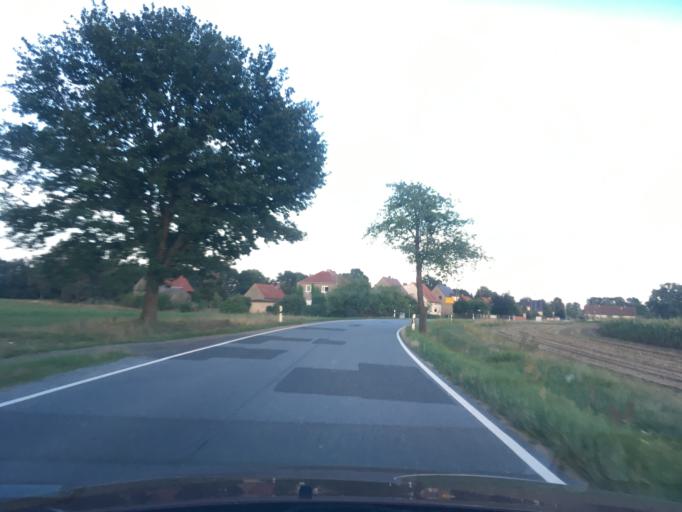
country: DE
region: Saxony
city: Rothenburg
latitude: 51.3164
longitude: 14.9898
